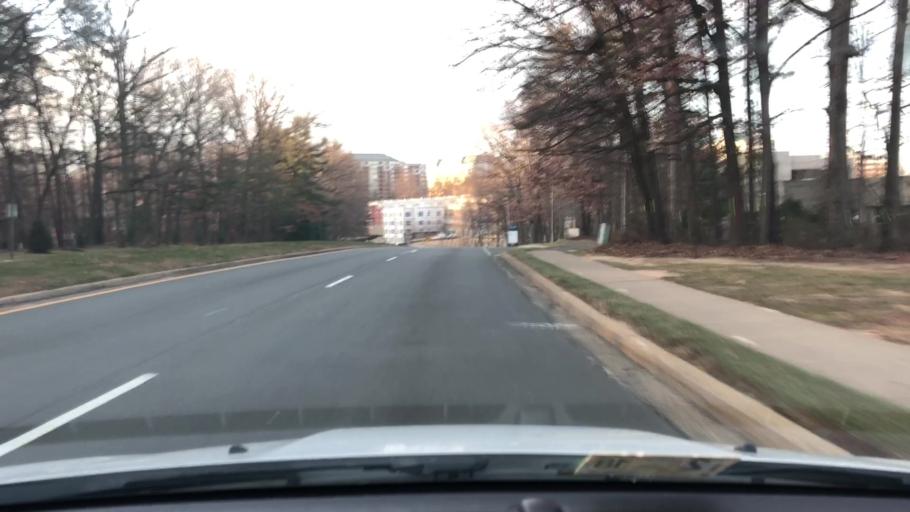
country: US
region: Virginia
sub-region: Fairfax County
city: Reston
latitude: 38.9462
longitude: -77.3478
